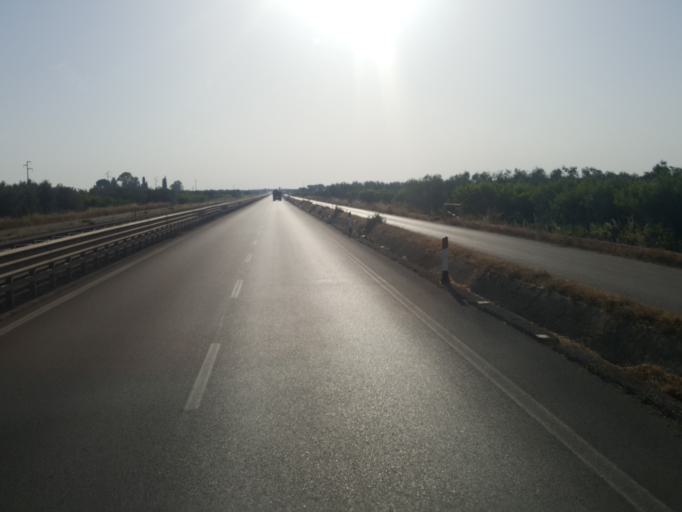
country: IT
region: Apulia
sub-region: Provincia di Barletta - Andria - Trani
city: San Ferdinando di Puglia
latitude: 41.3143
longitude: 16.1097
